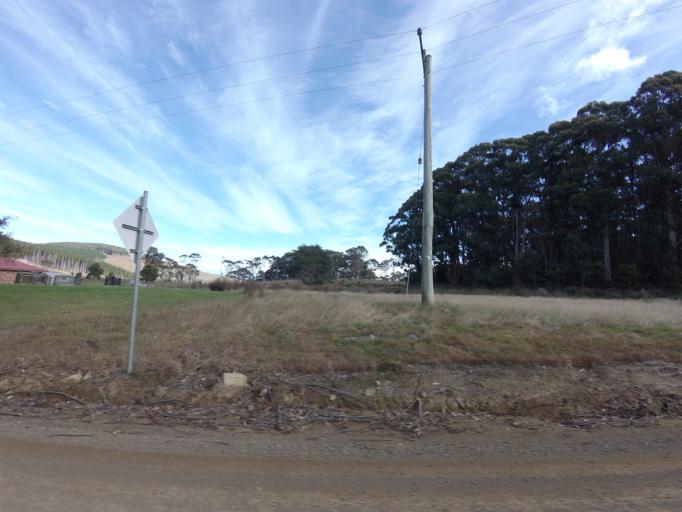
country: AU
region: Tasmania
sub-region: Clarence
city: Sandford
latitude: -43.1690
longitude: 147.7681
